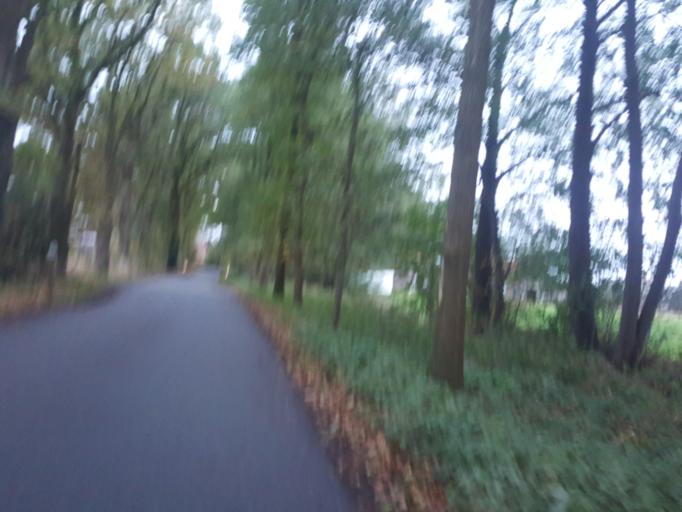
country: DE
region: Lower Saxony
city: Rastede
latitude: 53.1920
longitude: 8.1679
